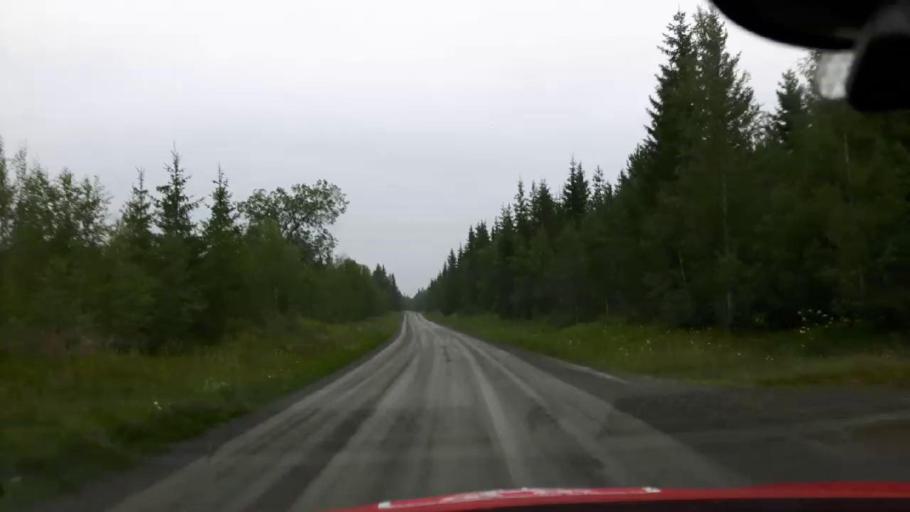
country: SE
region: Jaemtland
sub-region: OEstersunds Kommun
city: Brunflo
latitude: 62.9749
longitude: 14.8321
